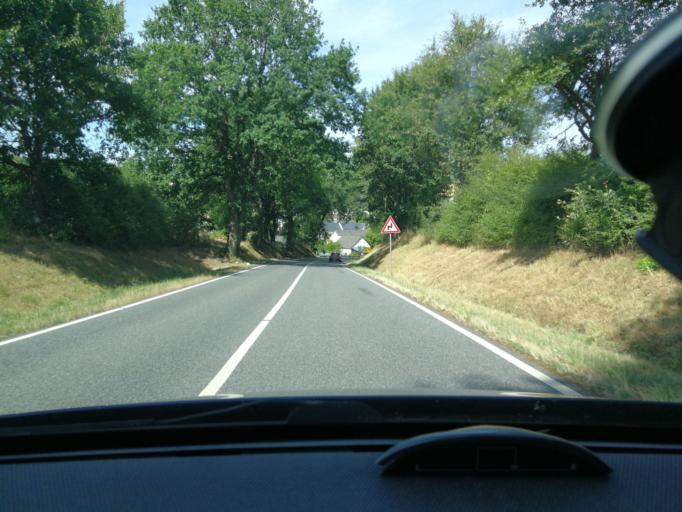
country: DE
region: Rheinland-Pfalz
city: Arenrath
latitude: 49.9504
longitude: 6.7422
